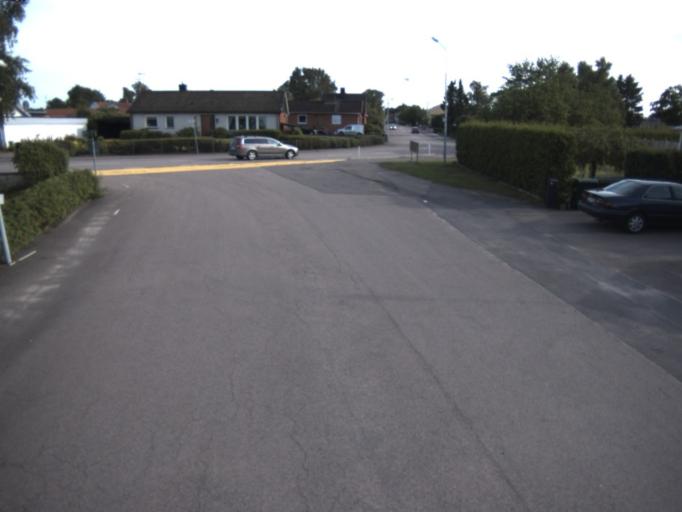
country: SE
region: Skane
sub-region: Helsingborg
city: Odakra
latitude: 56.1078
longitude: 12.7494
